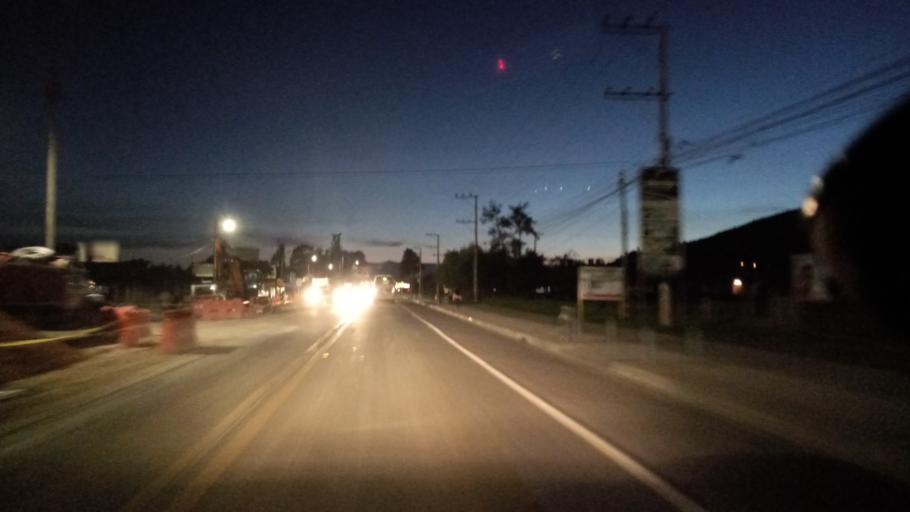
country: CO
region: Cundinamarca
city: Cota
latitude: 4.8018
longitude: -74.1087
